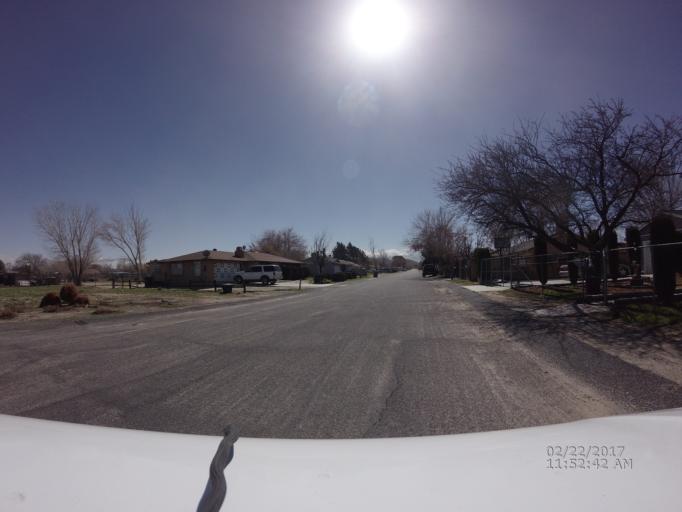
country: US
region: California
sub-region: Los Angeles County
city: Lake Los Angeles
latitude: 34.6229
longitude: -117.8195
